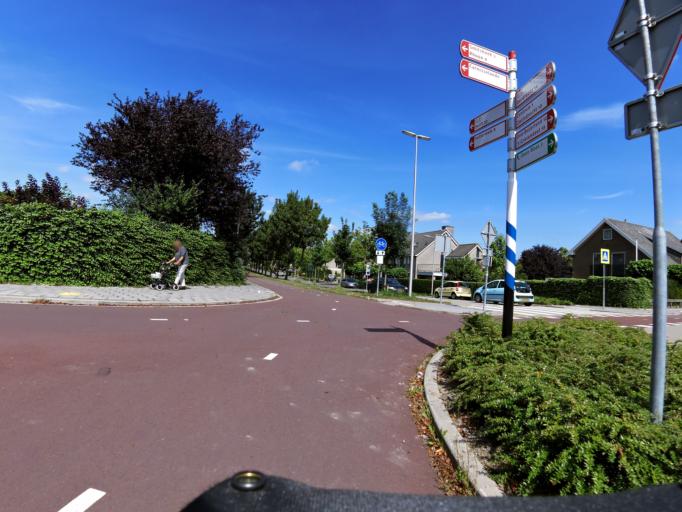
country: NL
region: South Holland
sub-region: Gemeente Barendrecht
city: Barendrecht
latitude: 51.8590
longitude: 4.5287
